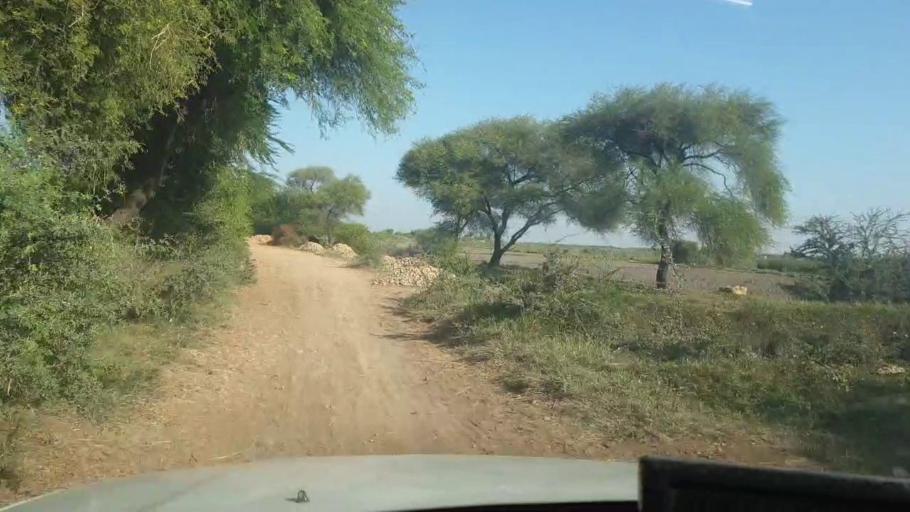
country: PK
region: Sindh
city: Mirpur Sakro
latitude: 24.4999
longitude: 67.6246
